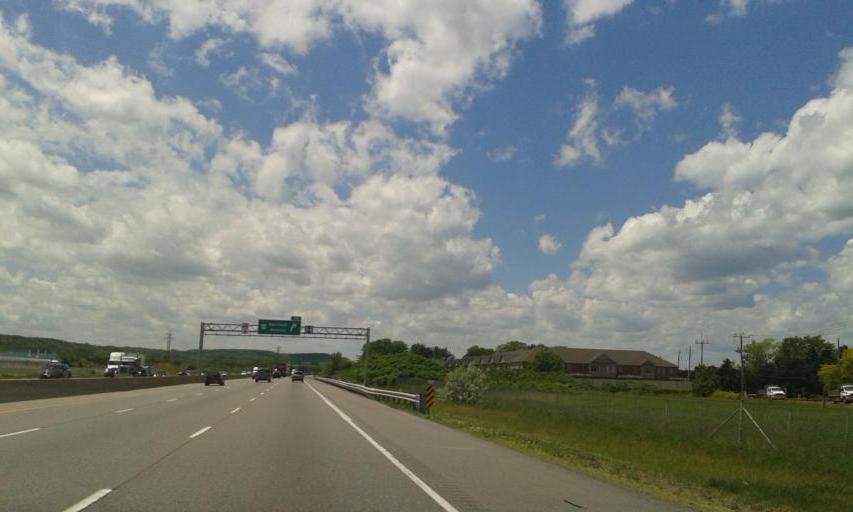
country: CA
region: Ontario
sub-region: Regional Municipality of Niagara
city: St. Catharines
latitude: 43.1894
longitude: -79.5107
